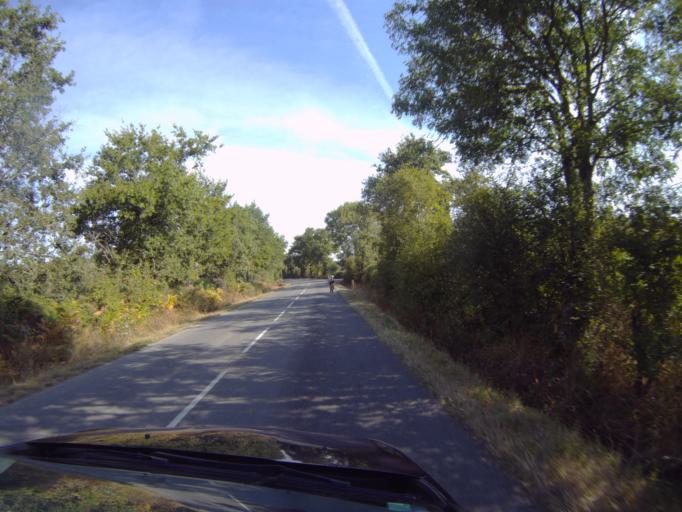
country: FR
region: Pays de la Loire
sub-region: Departement de la Vendee
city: Les Clouzeaux
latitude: 46.6085
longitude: -1.5021
